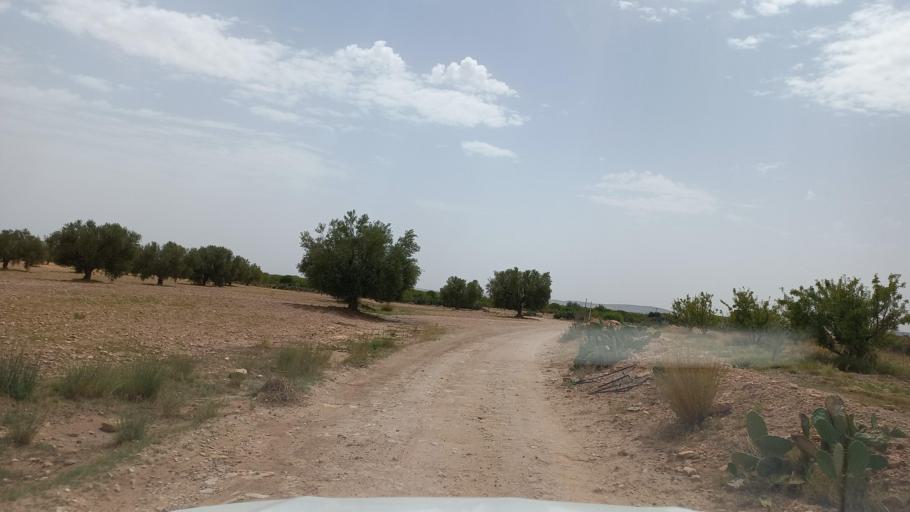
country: TN
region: Al Qasrayn
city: Kasserine
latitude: 35.2916
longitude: 9.0205
